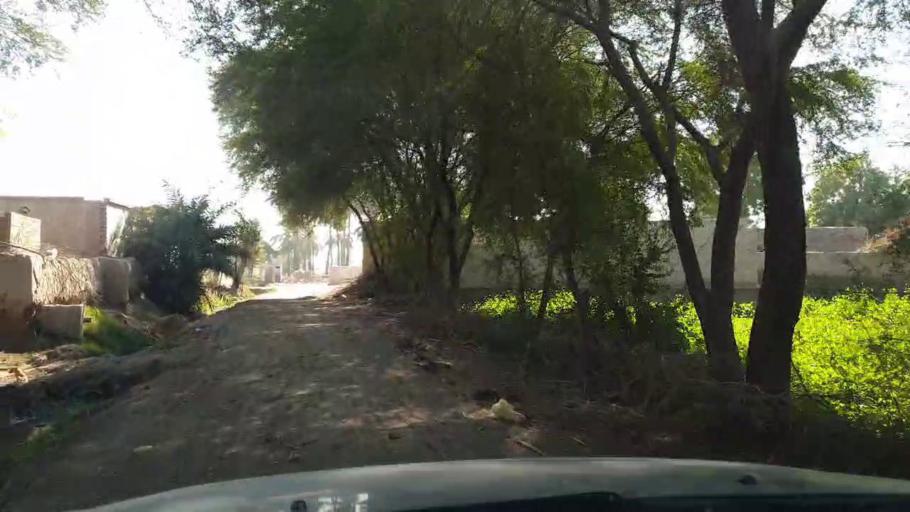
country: PK
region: Sindh
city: Ghotki
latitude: 28.0821
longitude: 69.3395
